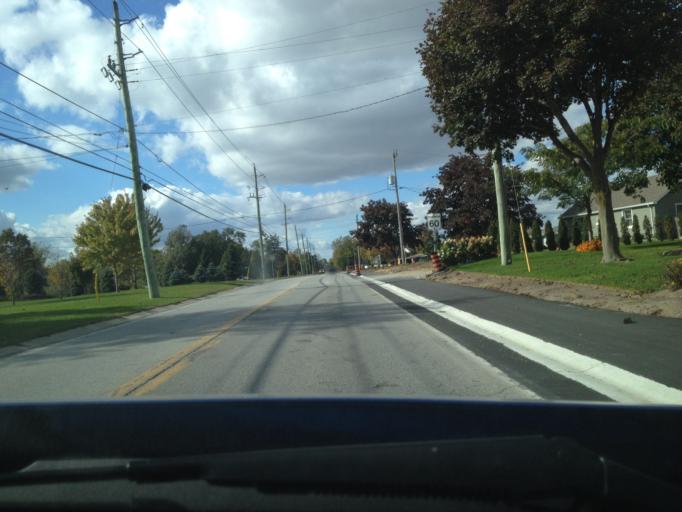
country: CA
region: Ontario
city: Amherstburg
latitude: 42.0355
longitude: -82.6318
